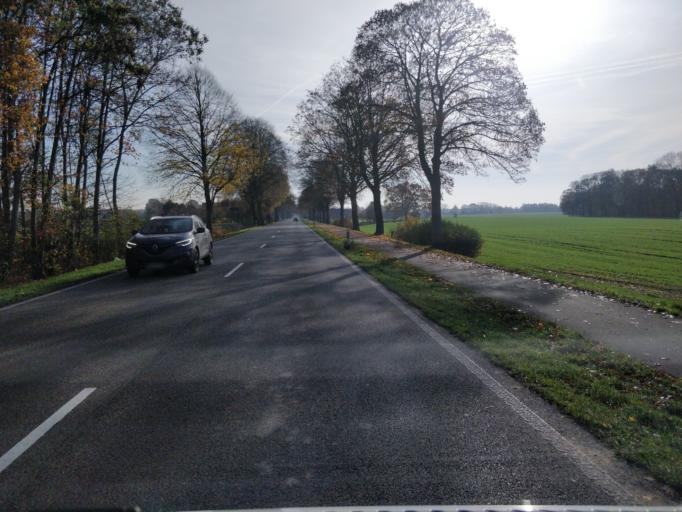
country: DE
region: North Rhine-Westphalia
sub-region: Regierungsbezirk Dusseldorf
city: Mehrhoog
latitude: 51.7328
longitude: 6.5026
